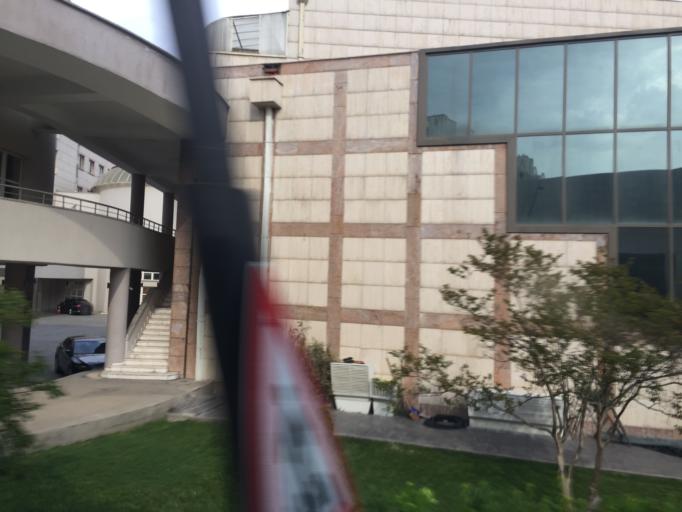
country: TR
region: Gaziantep
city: Gaziantep
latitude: 37.0662
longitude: 37.3728
